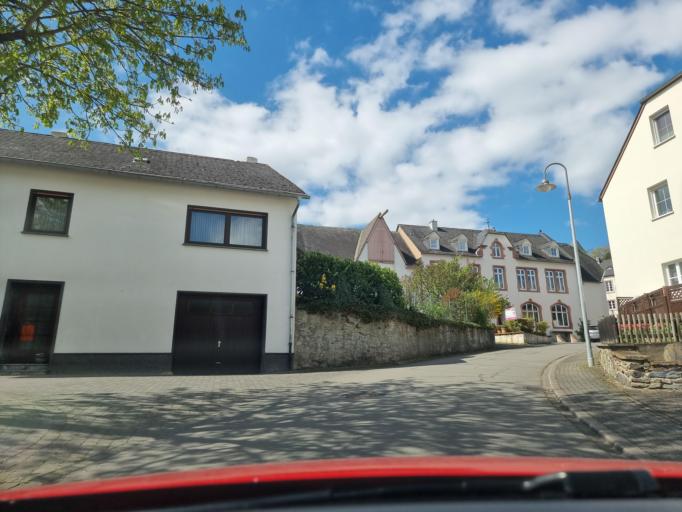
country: DE
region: Rheinland-Pfalz
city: Longuich
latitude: 49.7924
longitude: 6.7904
